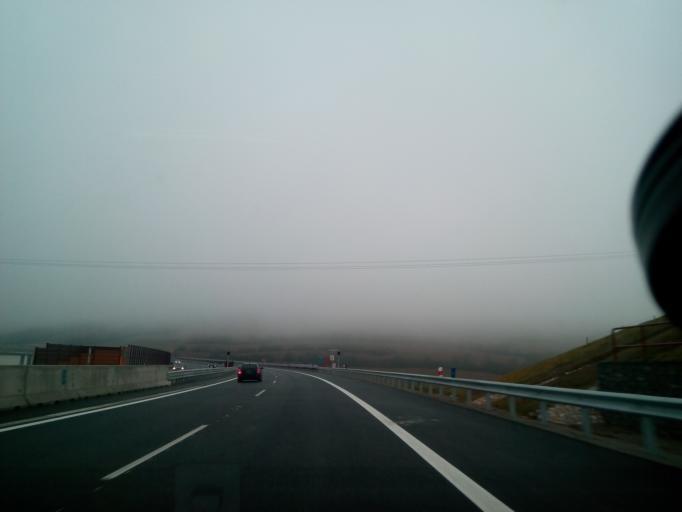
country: SK
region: Presovsky
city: Sabinov
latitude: 49.0006
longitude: 21.0582
